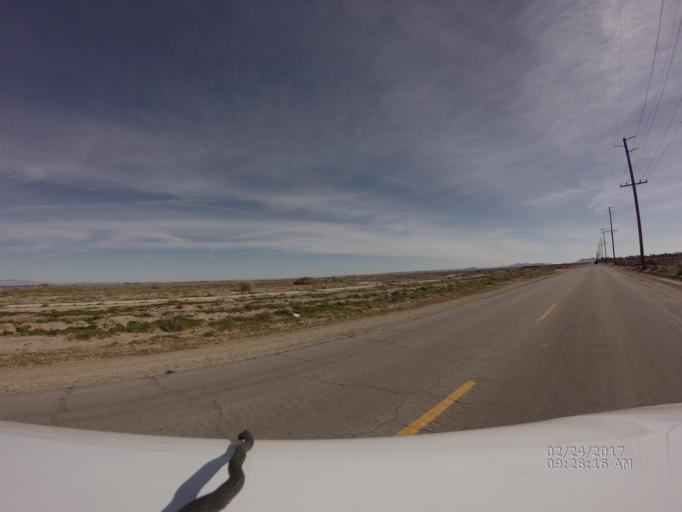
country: US
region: California
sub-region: Los Angeles County
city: Palmdale
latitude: 34.6313
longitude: -118.0509
